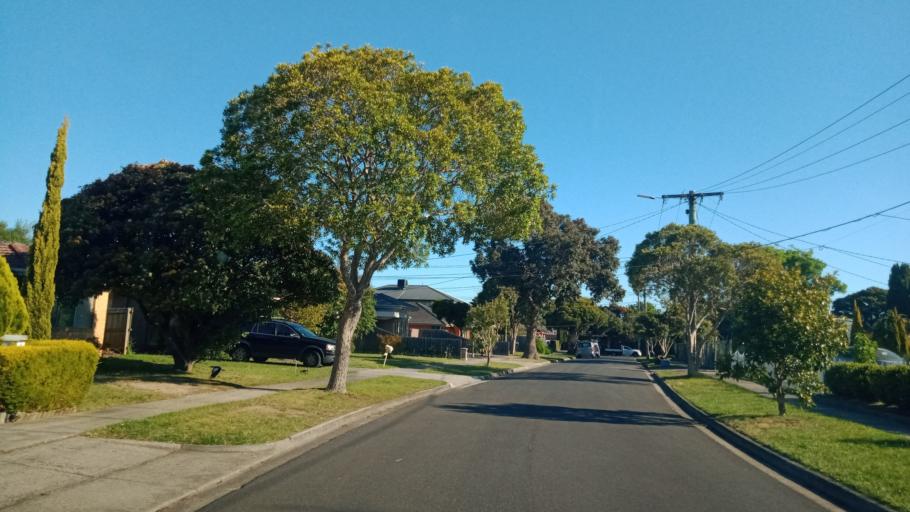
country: AU
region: Victoria
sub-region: Monash
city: Mulgrave
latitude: -37.9248
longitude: 145.1721
